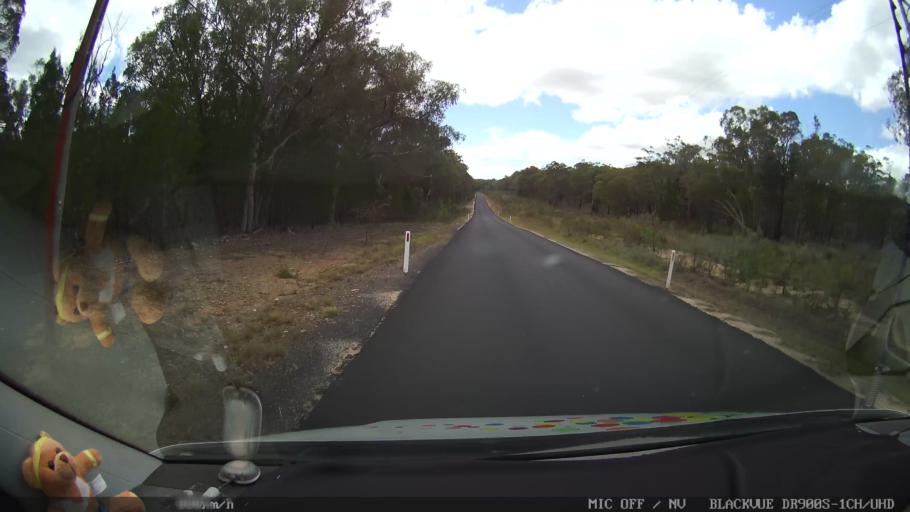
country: AU
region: New South Wales
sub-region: Glen Innes Severn
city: Glen Innes
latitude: -29.4401
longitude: 151.6199
